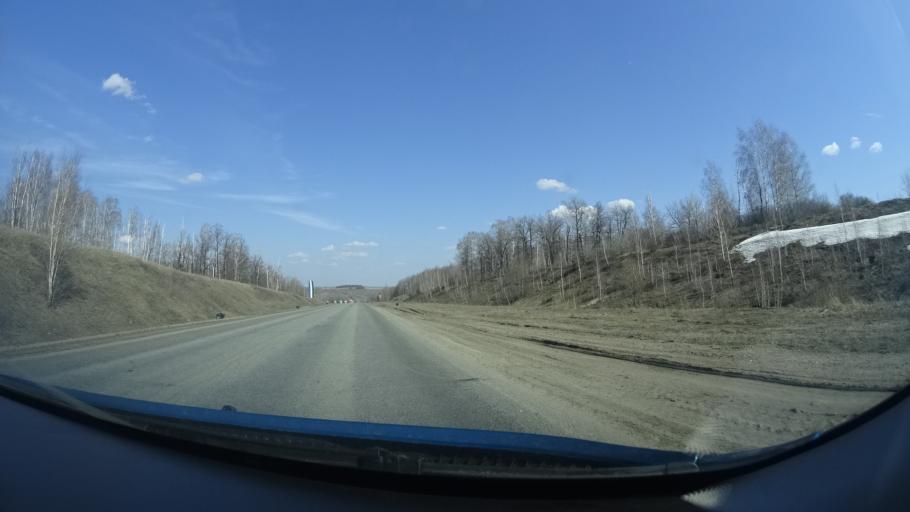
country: RU
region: Bashkortostan
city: Kandry
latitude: 54.5896
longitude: 54.2709
